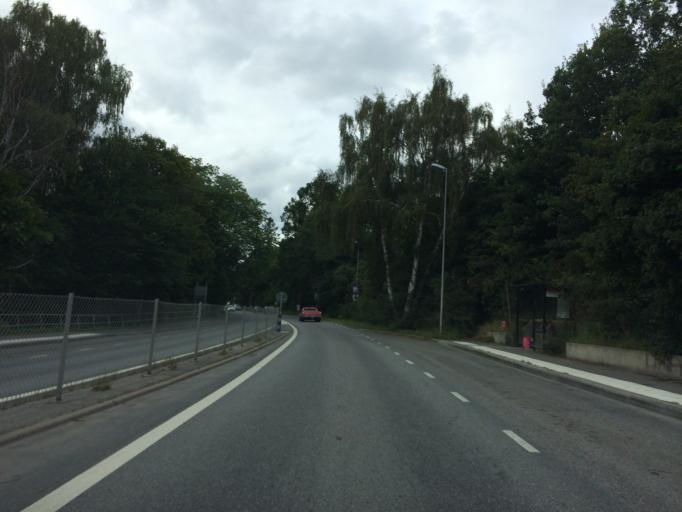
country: SE
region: Stockholm
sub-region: Sollentuna Kommun
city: Sollentuna
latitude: 59.4419
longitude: 17.9495
